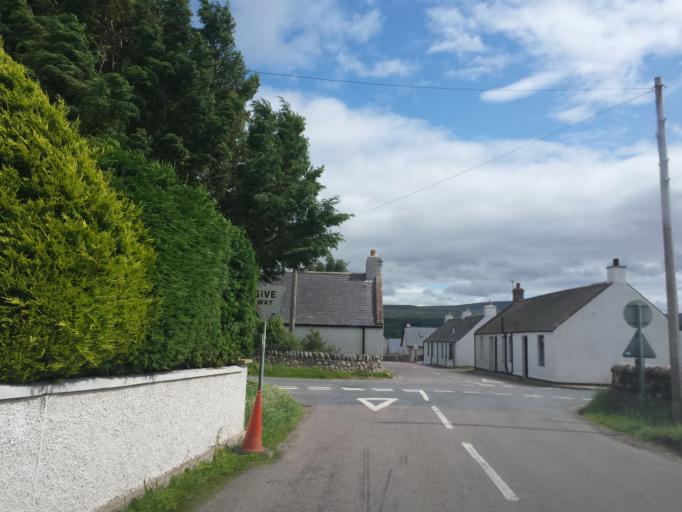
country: GB
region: Scotland
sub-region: Highland
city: Fortrose
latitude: 57.4792
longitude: -4.0854
